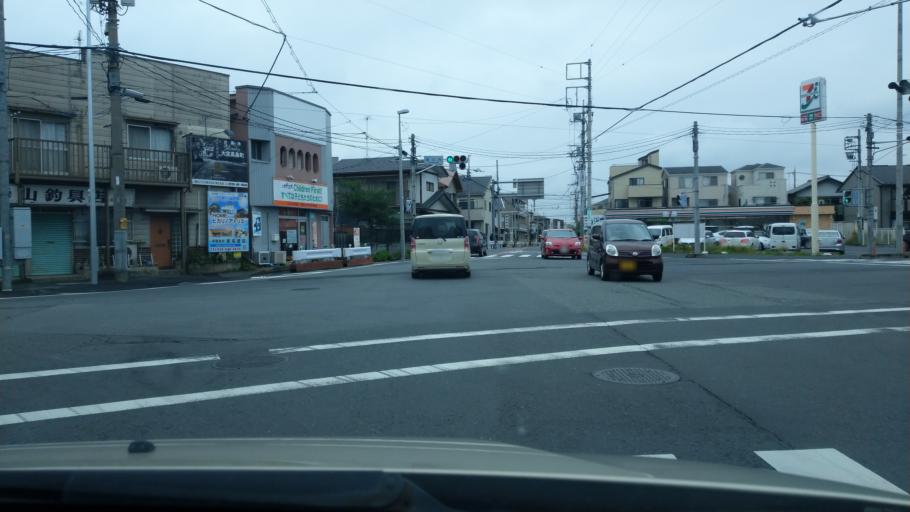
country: JP
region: Saitama
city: Saitama
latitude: 35.9113
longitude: 139.6337
